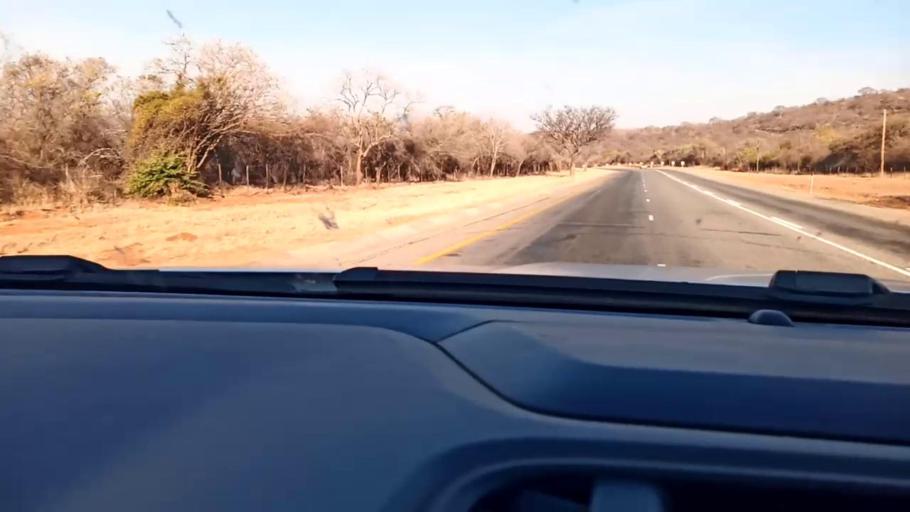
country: ZA
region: Limpopo
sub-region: Mopani District Municipality
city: Duiwelskloof
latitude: -23.6347
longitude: 30.1398
